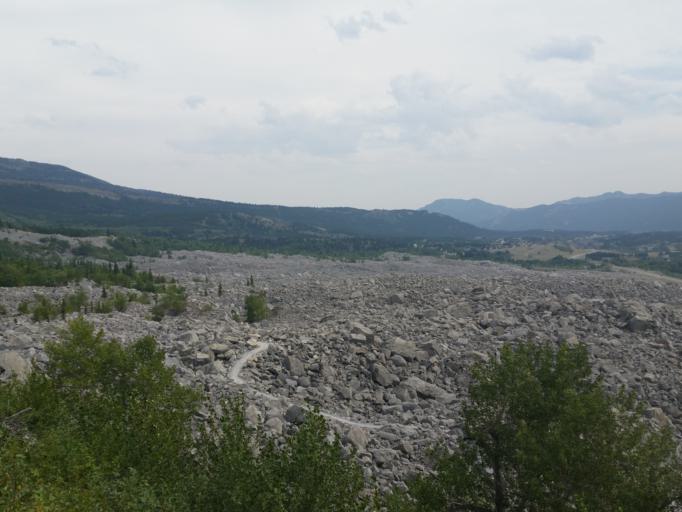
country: CA
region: Alberta
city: Pincher Creek
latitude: 49.5996
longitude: -114.3943
